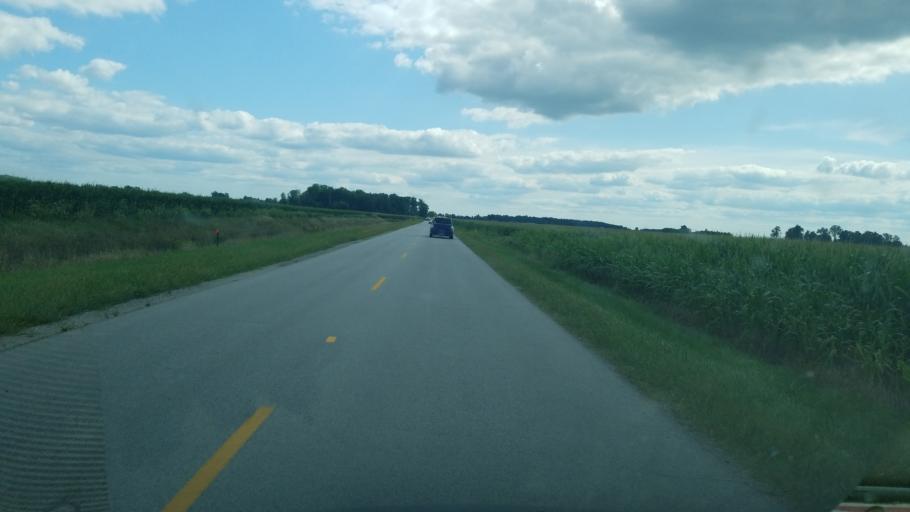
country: US
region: Ohio
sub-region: Logan County
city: Lakeview
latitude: 40.5677
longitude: -83.9757
